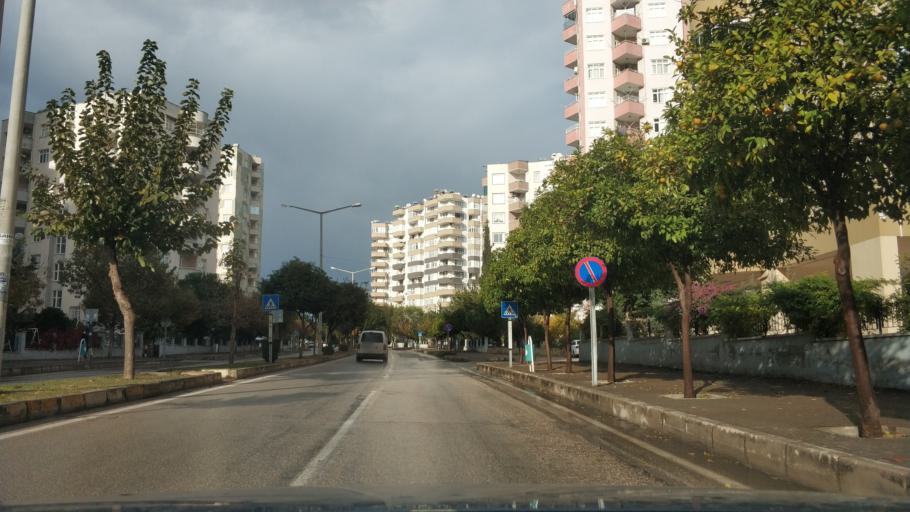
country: TR
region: Adana
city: Seyhan
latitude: 37.0359
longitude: 35.2614
